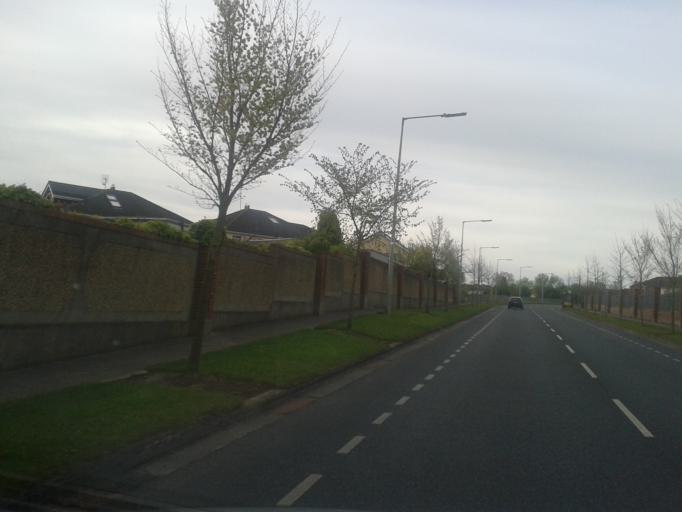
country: IE
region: Leinster
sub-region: Fingal County
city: Swords
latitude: 53.4651
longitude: -6.2397
